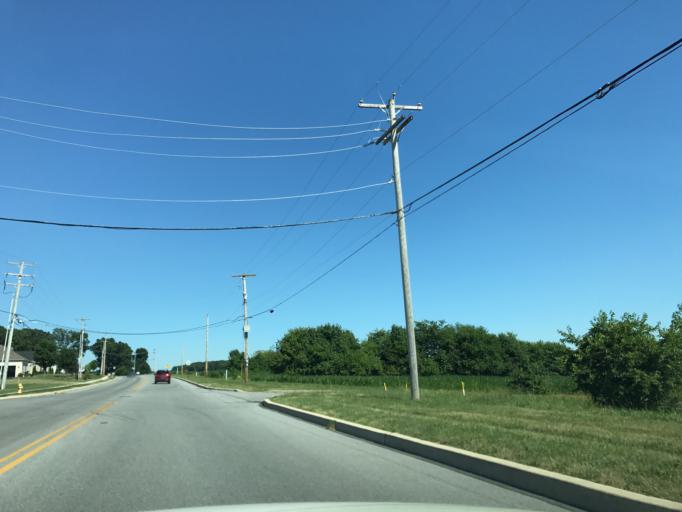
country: US
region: Pennsylvania
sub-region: York County
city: Parkville
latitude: 39.7685
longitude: -76.9787
